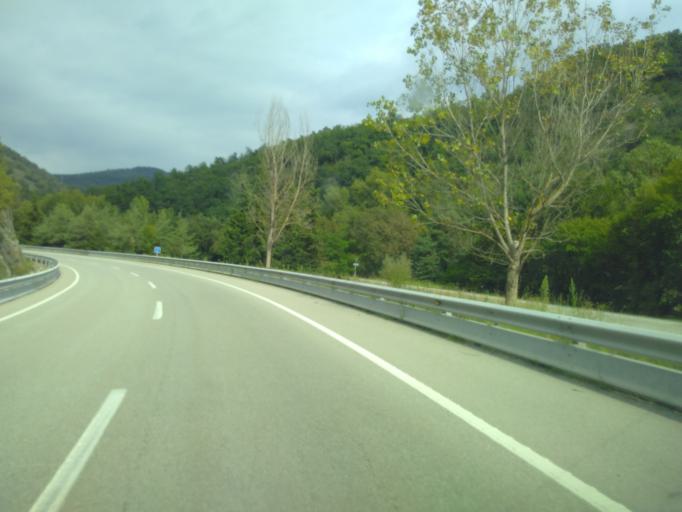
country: ES
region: Catalonia
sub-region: Provincia de Barcelona
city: Montesquiu
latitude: 42.1365
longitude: 2.2093
